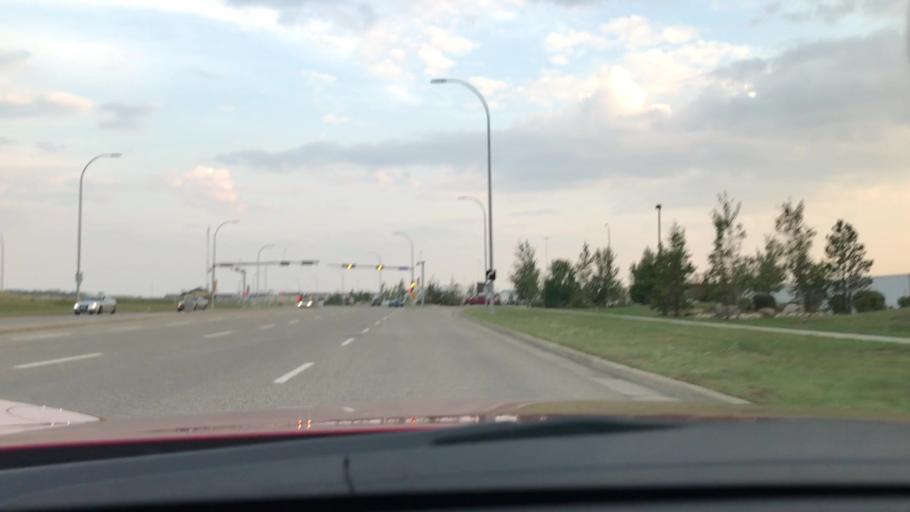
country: CA
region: Alberta
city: Airdrie
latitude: 51.2090
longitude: -113.9905
